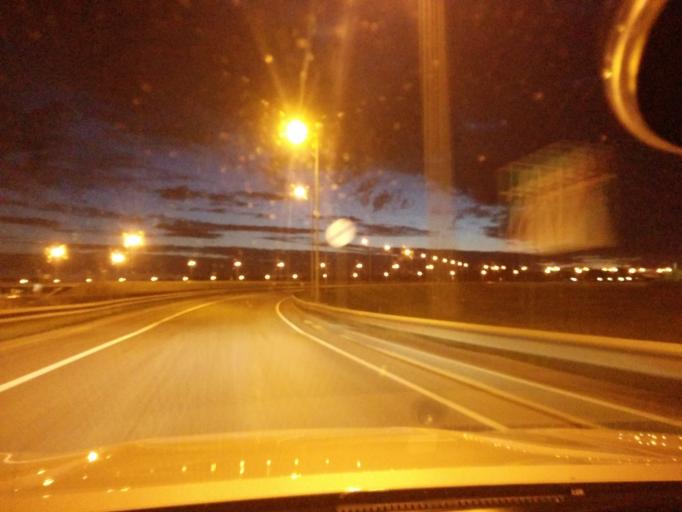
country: RU
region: Leningrad
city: Bugry
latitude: 60.0894
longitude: 30.3737
